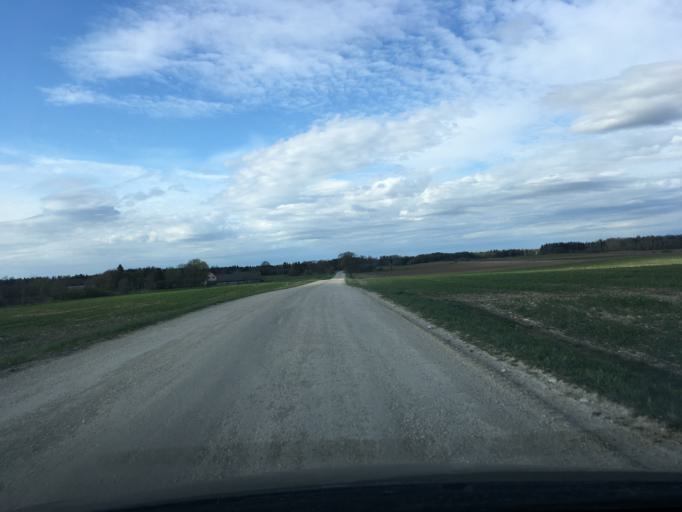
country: EE
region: Raplamaa
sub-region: Maerjamaa vald
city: Marjamaa
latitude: 58.9315
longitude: 24.3071
